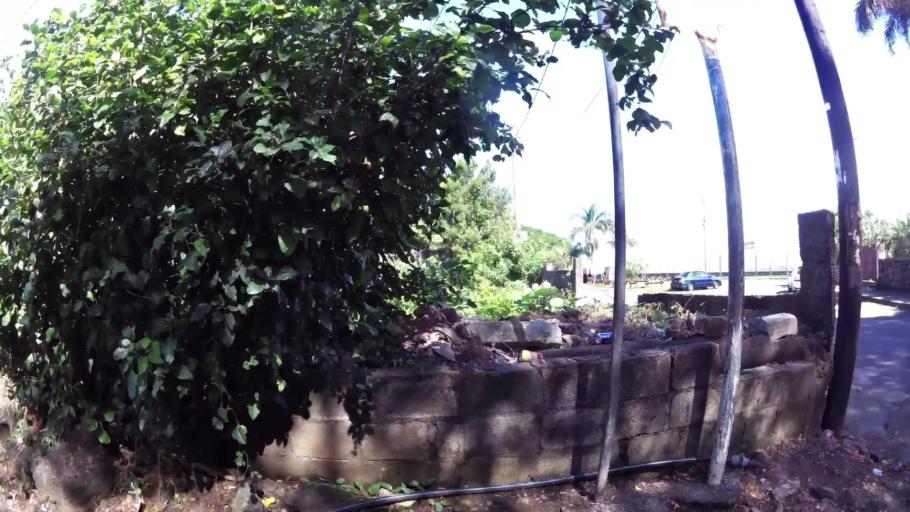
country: MU
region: Grand Port
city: Plaine Magnien
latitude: -20.4344
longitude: 57.6593
